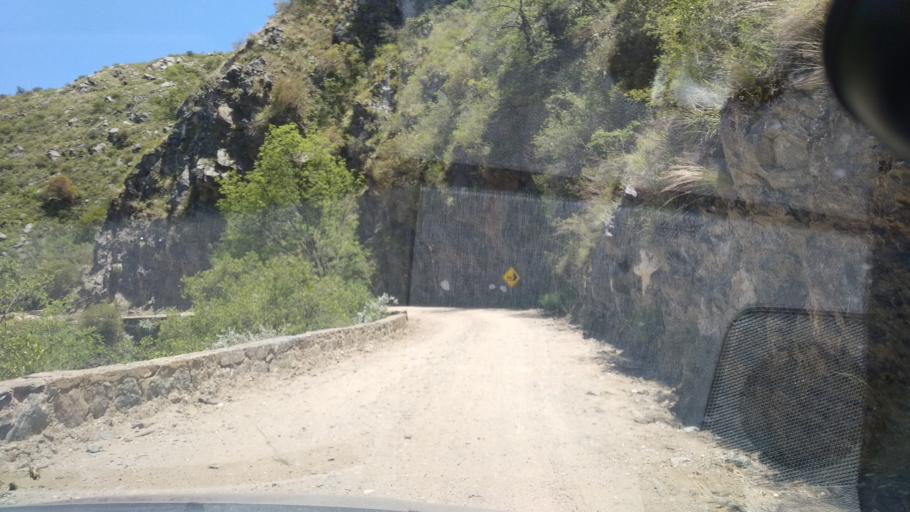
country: AR
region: Cordoba
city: Salsacate
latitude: -31.3784
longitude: -65.4051
